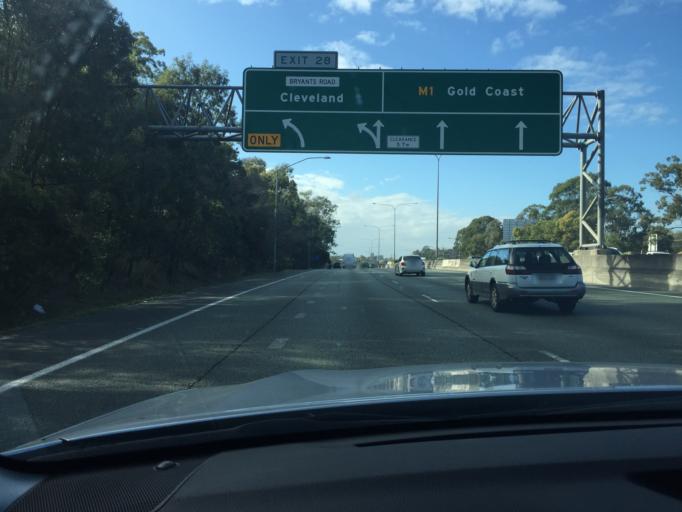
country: AU
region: Queensland
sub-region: Logan
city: Slacks Creek
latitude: -27.6531
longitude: 153.1618
